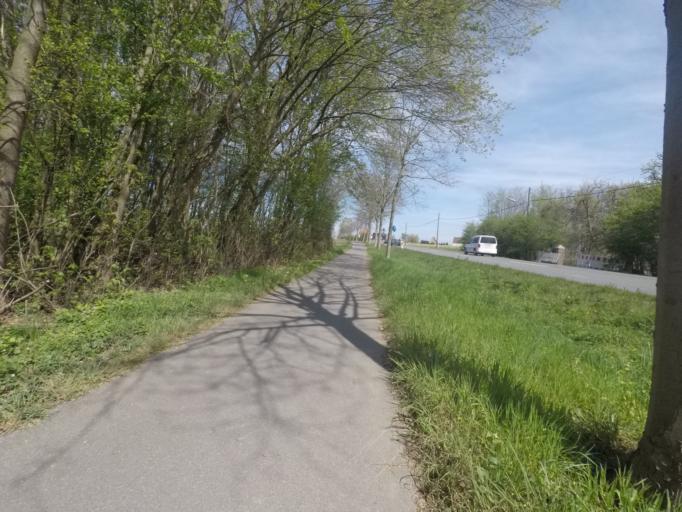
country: DE
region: North Rhine-Westphalia
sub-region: Regierungsbezirk Detmold
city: Leopoldshohe
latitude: 52.0508
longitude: 8.6362
